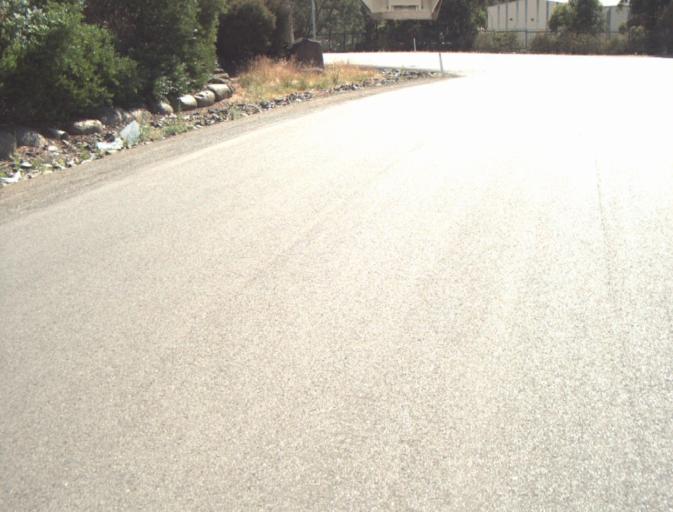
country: AU
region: Tasmania
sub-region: Launceston
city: Summerhill
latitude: -41.4802
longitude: 147.1539
